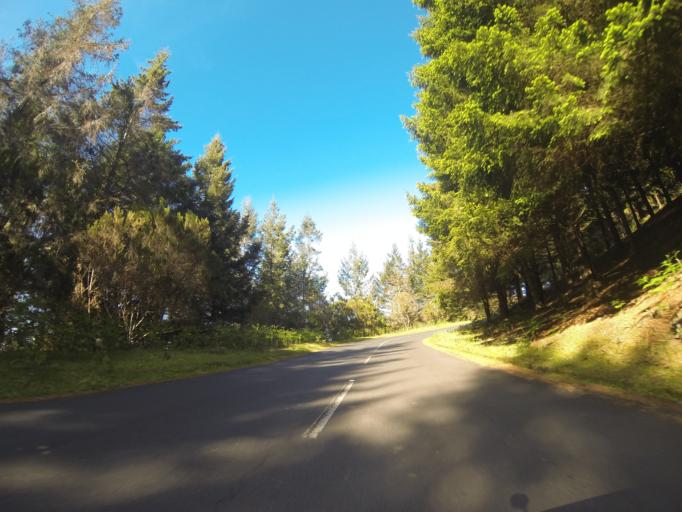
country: PT
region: Madeira
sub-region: Funchal
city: Nossa Senhora do Monte
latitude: 32.7185
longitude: -16.8847
